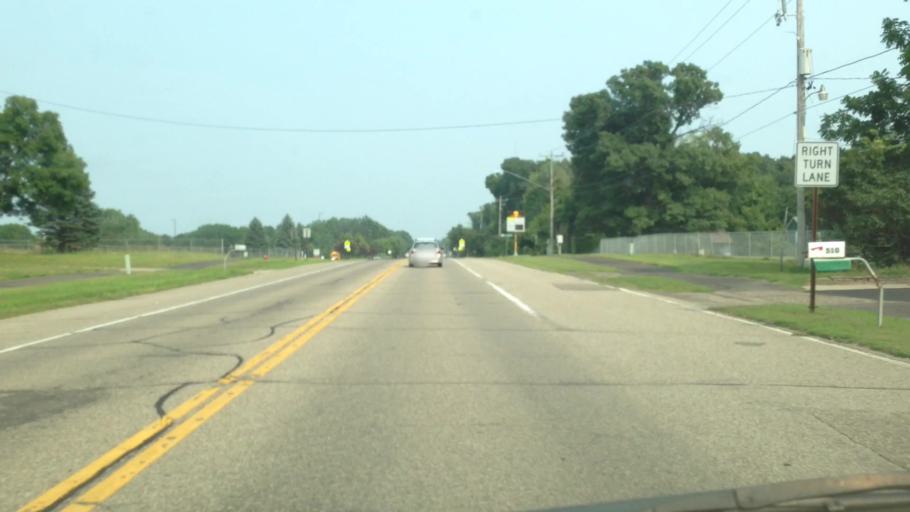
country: US
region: Minnesota
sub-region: Anoka County
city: Lino Lakes
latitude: 45.1422
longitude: -93.1168
